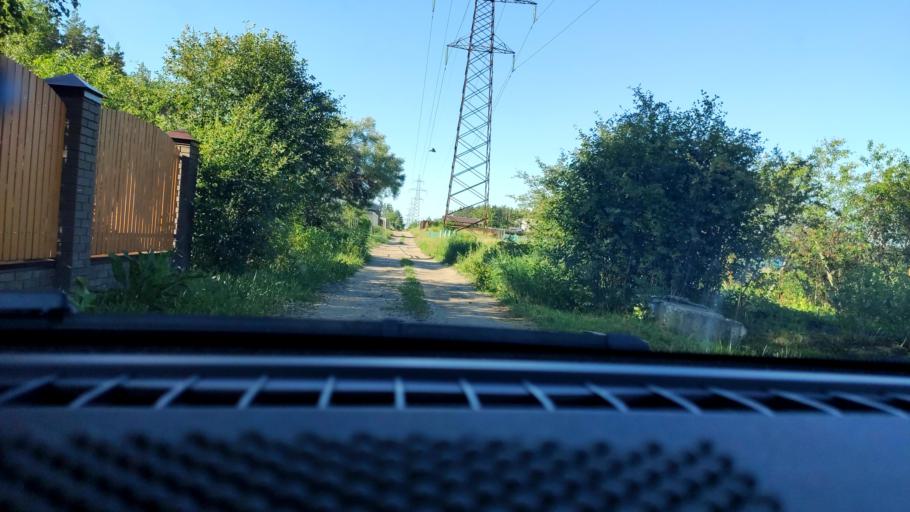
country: RU
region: Voronezj
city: Volya
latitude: 51.7444
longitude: 39.4611
